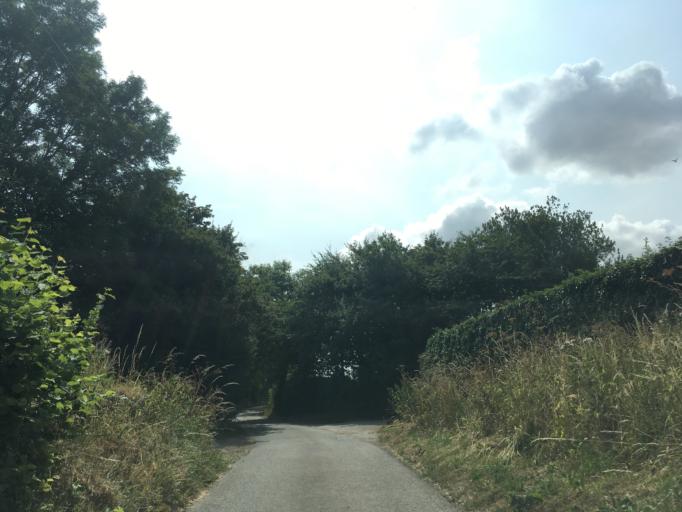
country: GB
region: England
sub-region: Gloucestershire
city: Nailsworth
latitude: 51.6754
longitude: -2.2288
